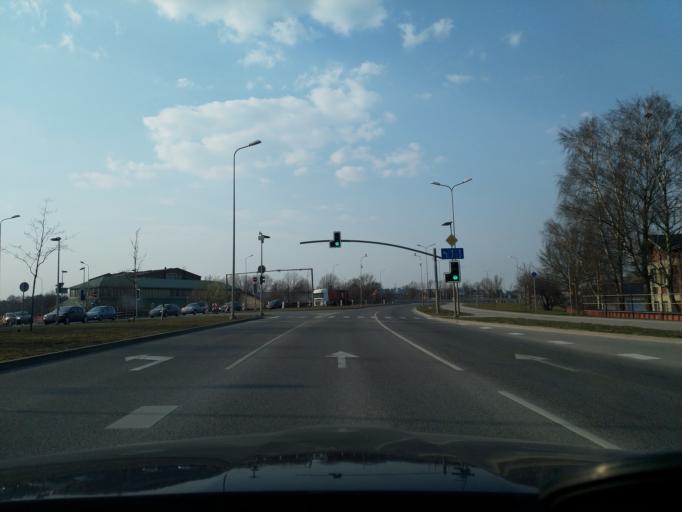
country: LV
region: Liepaja
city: Liepaja
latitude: 56.5110
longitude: 21.0229
